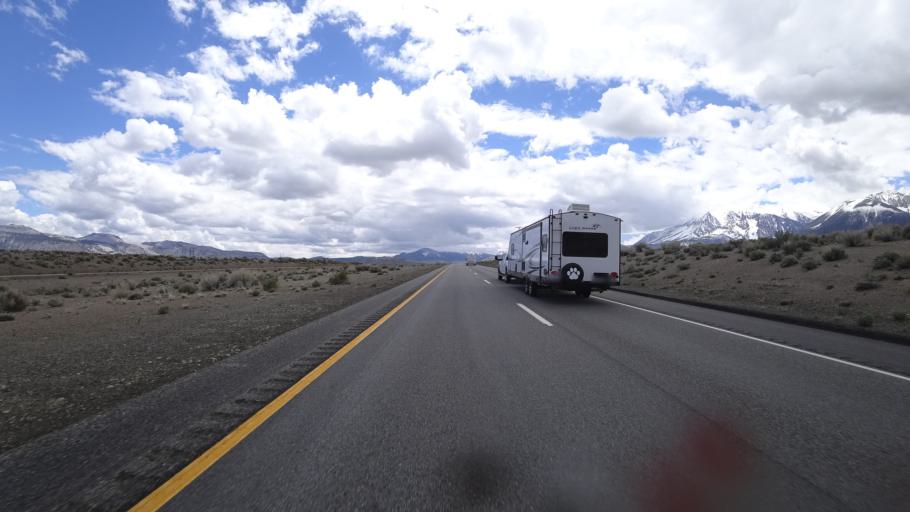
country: US
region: California
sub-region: Mono County
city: Mammoth Lakes
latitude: 37.9061
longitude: -119.0950
